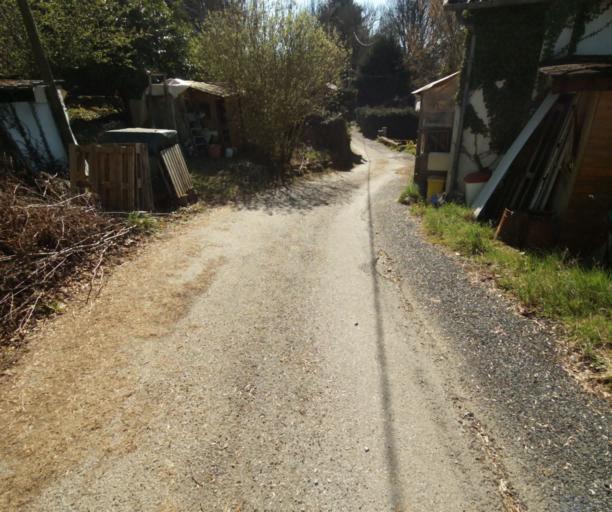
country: FR
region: Limousin
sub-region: Departement de la Correze
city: Treignac
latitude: 45.4794
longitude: 1.7718
